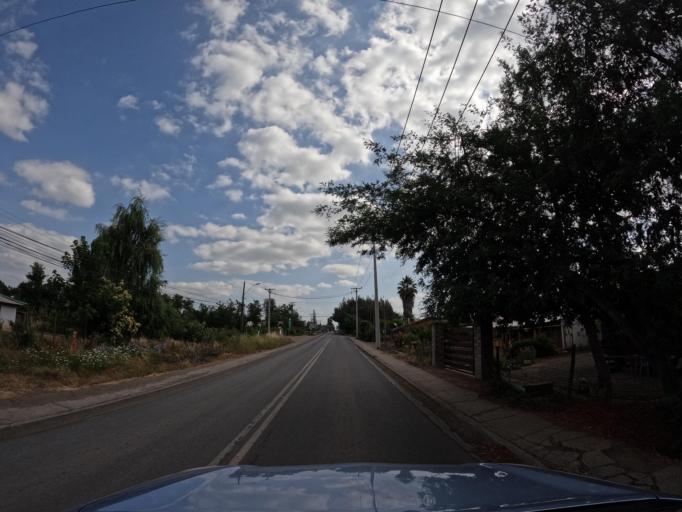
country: CL
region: Maule
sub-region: Provincia de Curico
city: Molina
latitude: -35.1591
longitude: -71.2855
